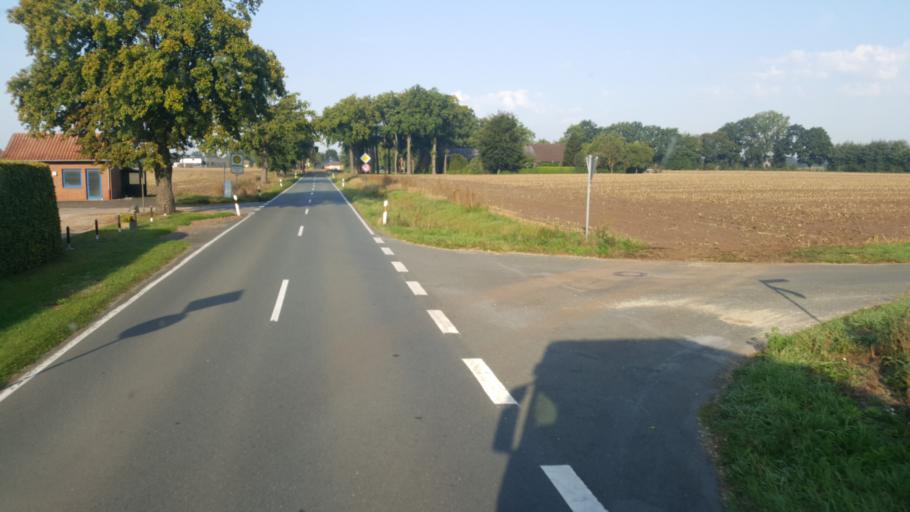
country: DE
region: North Rhine-Westphalia
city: Rietberg
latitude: 51.7380
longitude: 8.4021
